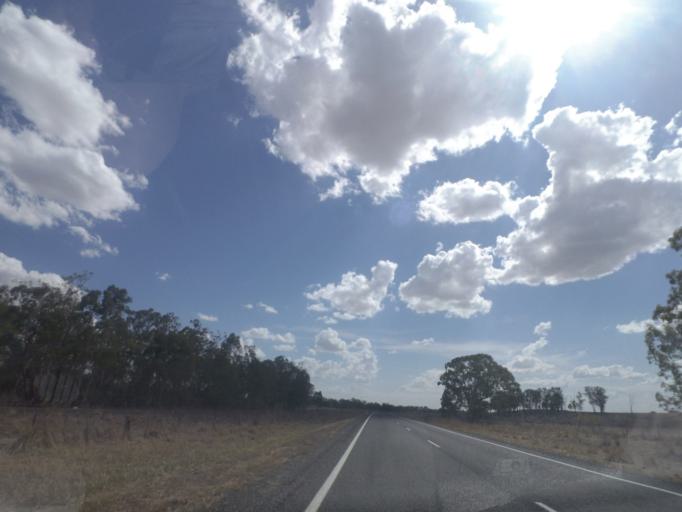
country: AU
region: Queensland
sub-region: Southern Downs
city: Stanthorpe
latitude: -28.3906
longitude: 151.3220
